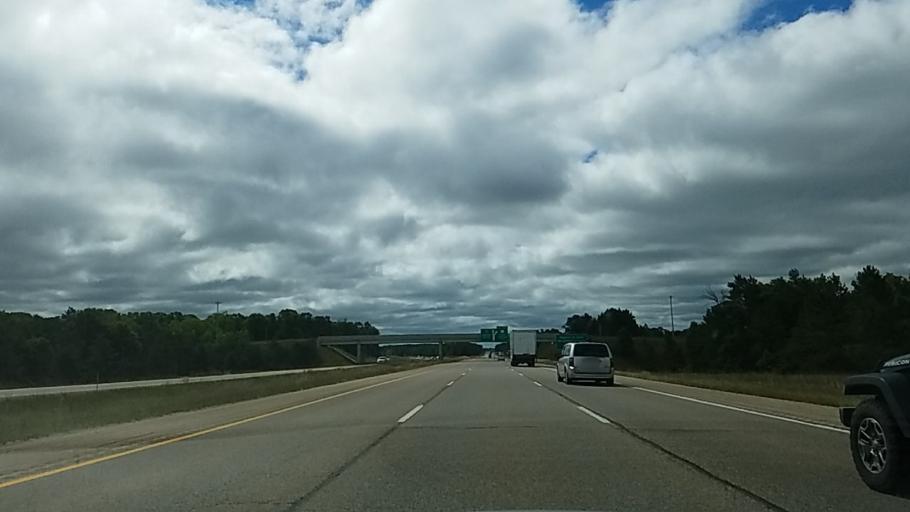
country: US
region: Michigan
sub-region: Crawford County
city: Grayling
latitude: 44.6003
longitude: -84.7094
